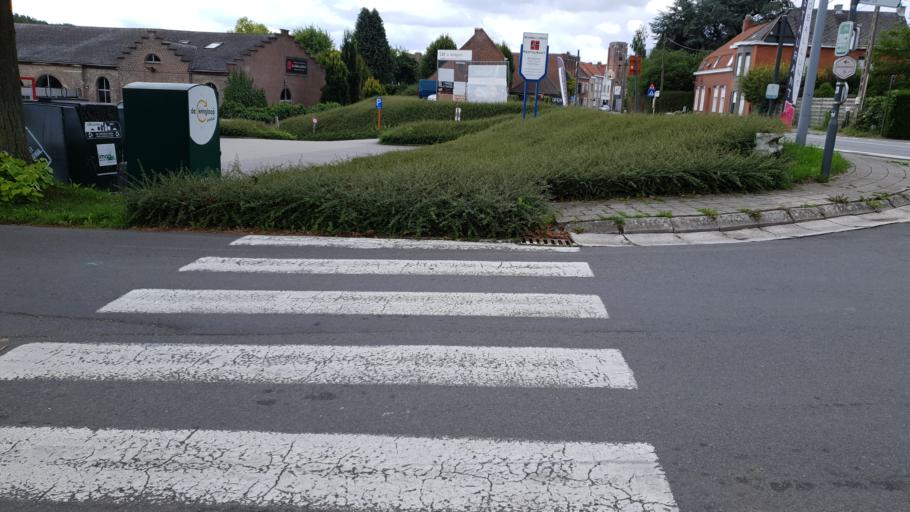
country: BE
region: Flanders
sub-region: Provincie West-Vlaanderen
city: Avelgem
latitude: 50.7486
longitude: 3.4115
